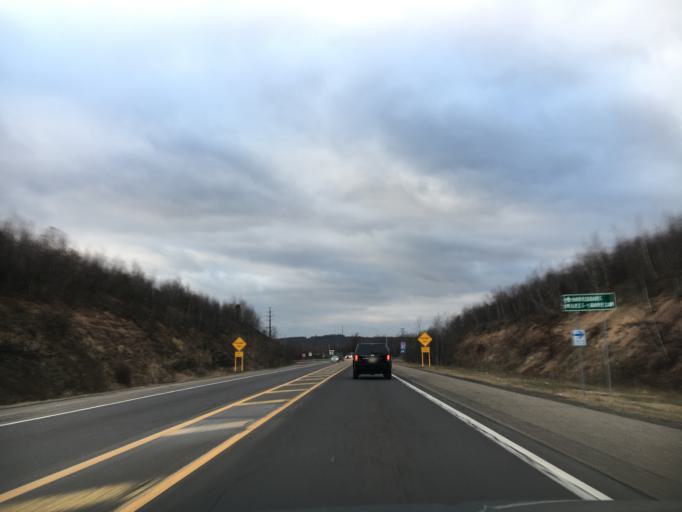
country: US
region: Pennsylvania
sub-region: Schuylkill County
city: McAdoo
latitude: 40.9256
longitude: -76.0078
